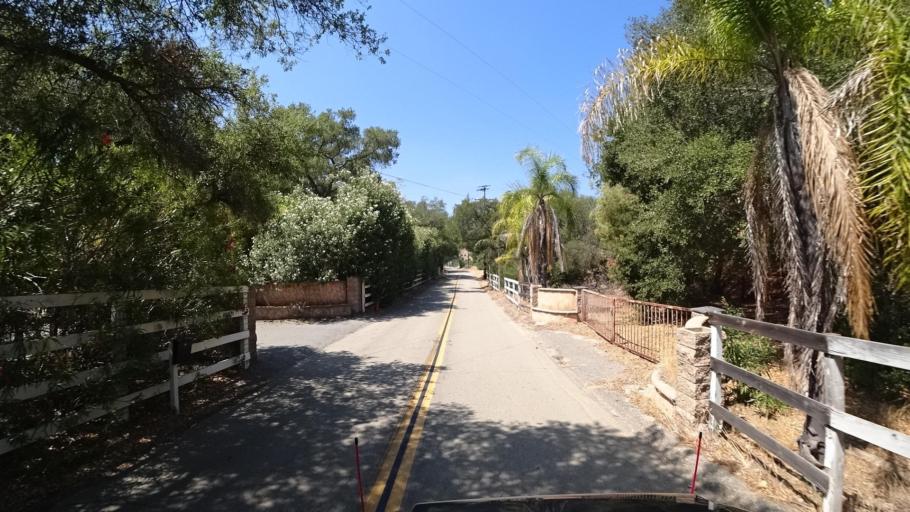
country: US
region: California
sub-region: San Diego County
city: Fallbrook
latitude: 33.4559
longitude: -117.2984
